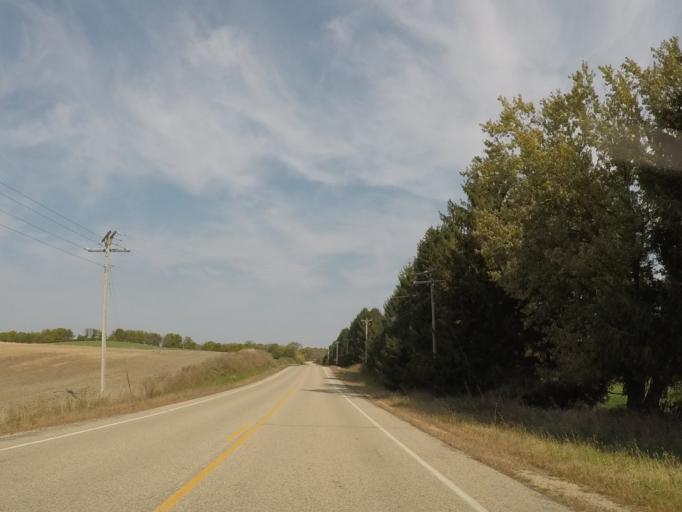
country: US
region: Wisconsin
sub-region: Dane County
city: Cross Plains
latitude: 43.0386
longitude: -89.6162
